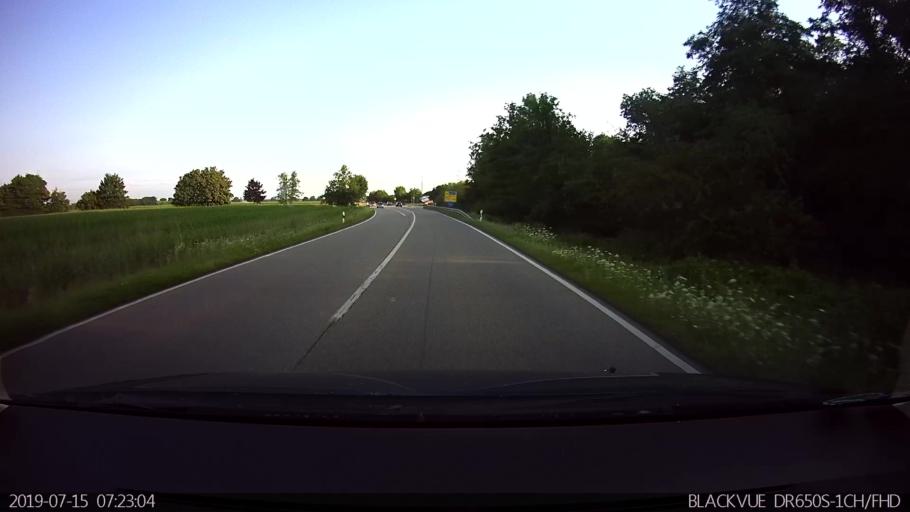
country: DE
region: Baden-Wuerttemberg
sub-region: Freiburg Region
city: Unterkrozingen
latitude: 47.9387
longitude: 7.6837
